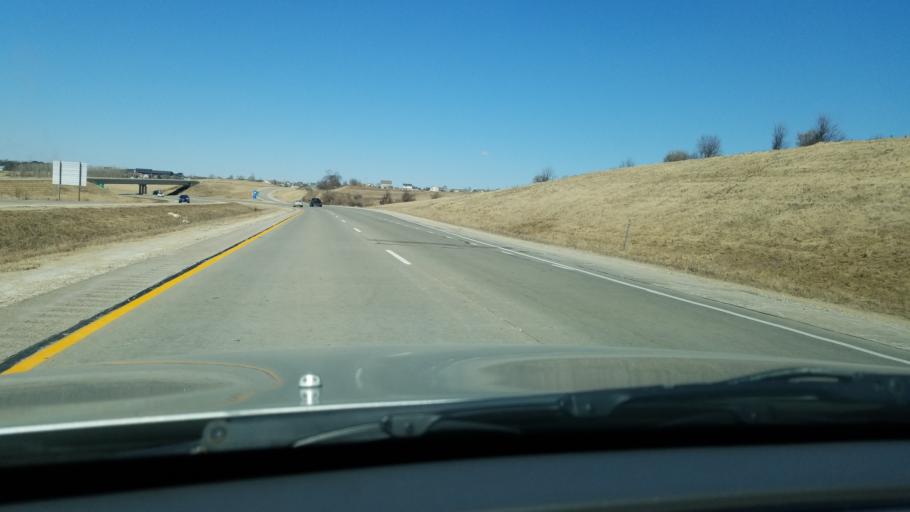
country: US
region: Wisconsin
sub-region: Dane County
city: Verona
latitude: 42.9813
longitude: -89.5570
